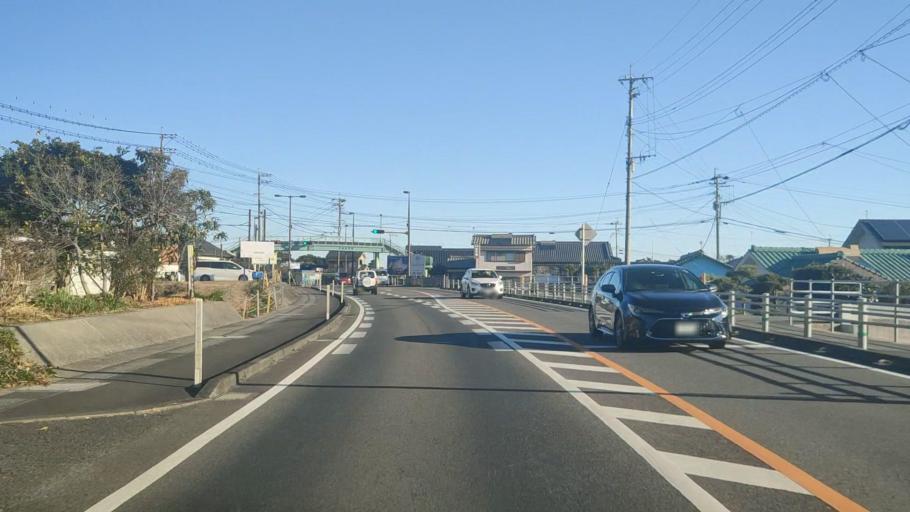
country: JP
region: Miyazaki
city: Nobeoka
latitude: 32.3717
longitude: 131.6304
